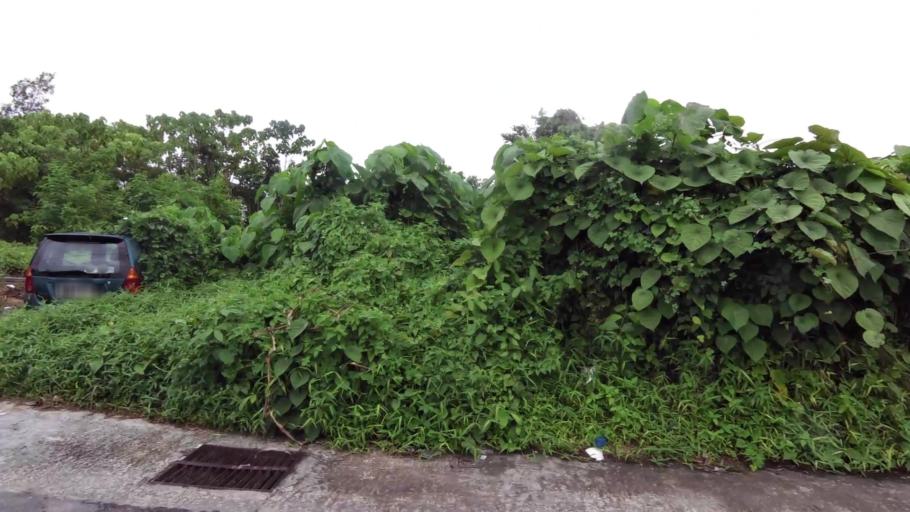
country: BN
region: Brunei and Muara
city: Bandar Seri Begawan
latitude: 4.8960
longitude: 114.9278
